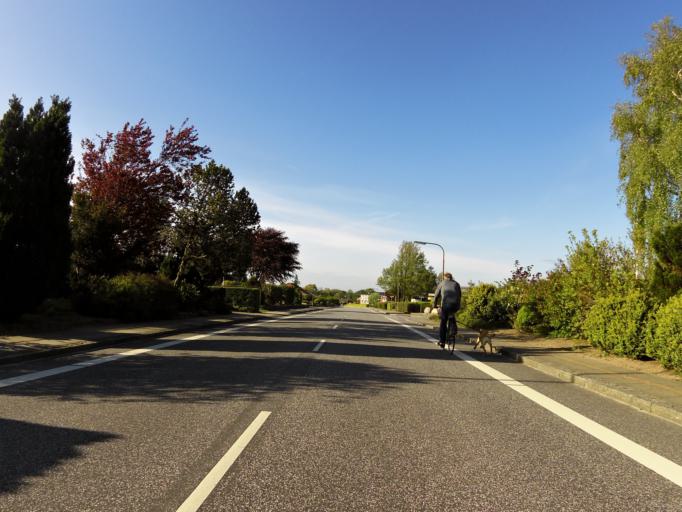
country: DK
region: South Denmark
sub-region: Tonder Kommune
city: Toftlund
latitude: 55.1833
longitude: 9.0628
